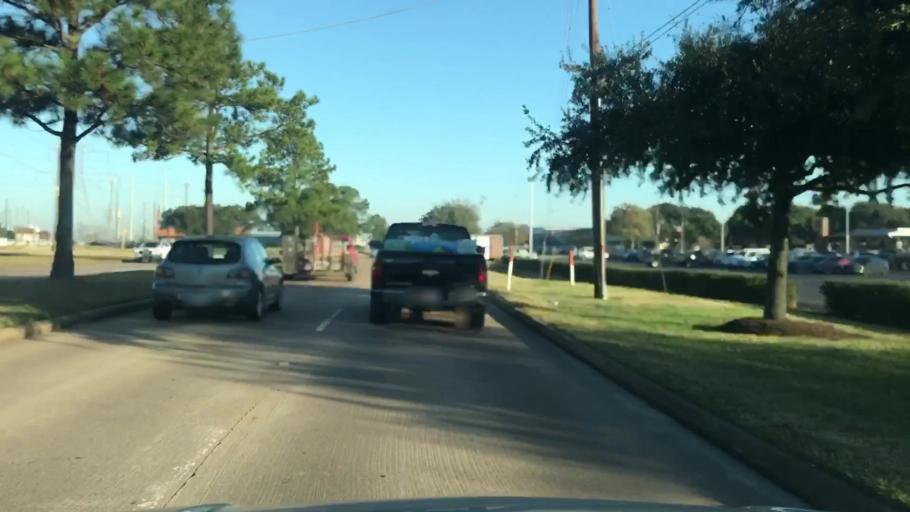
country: US
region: Texas
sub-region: Fort Bend County
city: Cinco Ranch
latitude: 29.7969
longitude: -95.7518
